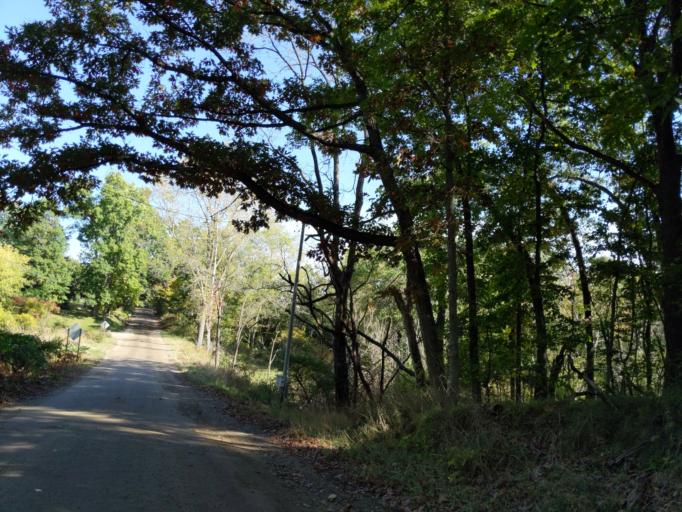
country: US
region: Michigan
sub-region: Clinton County
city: Bath
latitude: 42.8059
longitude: -84.4471
